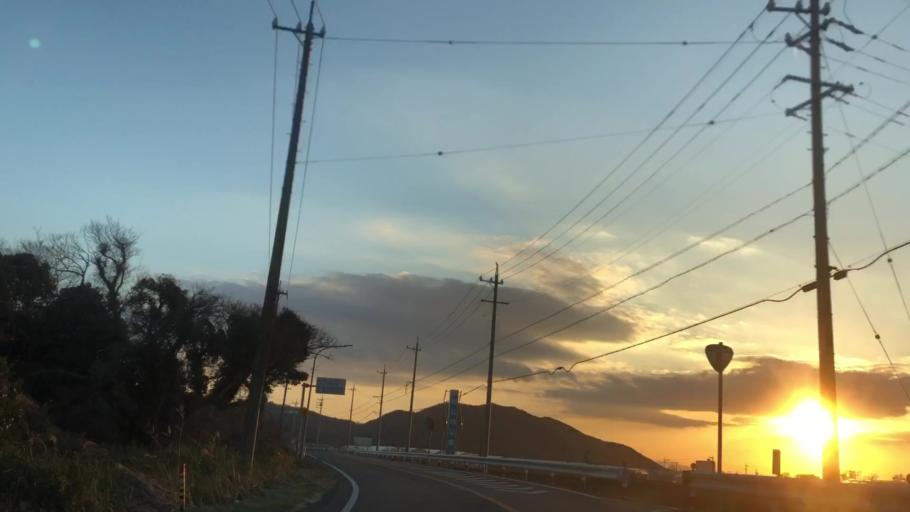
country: JP
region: Aichi
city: Toyohama
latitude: 34.5989
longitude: 137.0502
